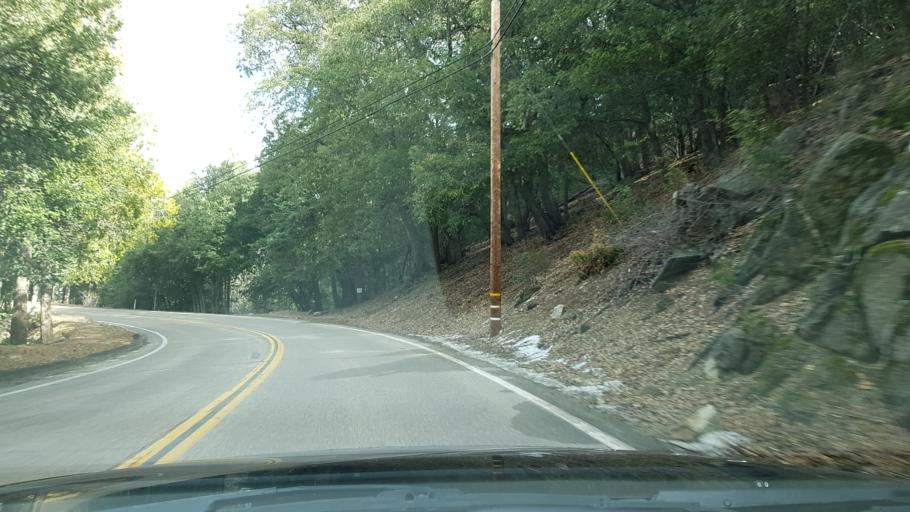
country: US
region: California
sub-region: Riverside County
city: Aguanga
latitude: 33.3535
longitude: -116.8706
